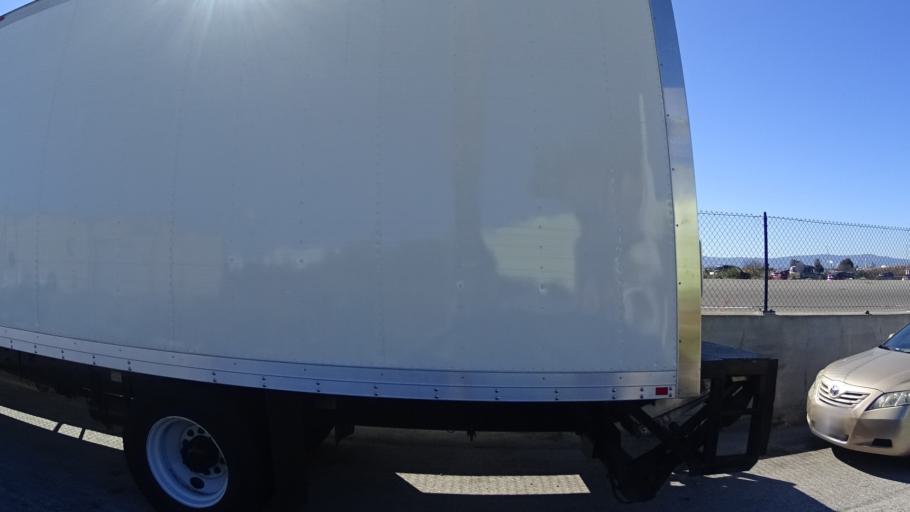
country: US
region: California
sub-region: Santa Clara County
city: Santa Clara
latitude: 37.3767
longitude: -121.9394
